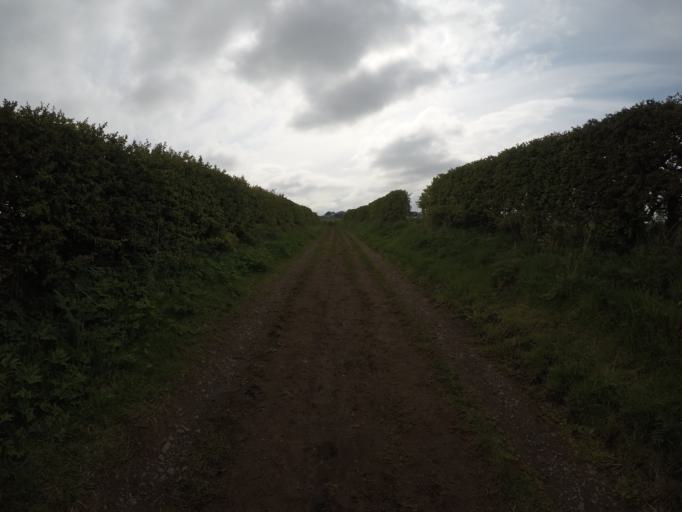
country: GB
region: Scotland
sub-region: East Renfrewshire
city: Newton Mearns
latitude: 55.7625
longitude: -4.3113
